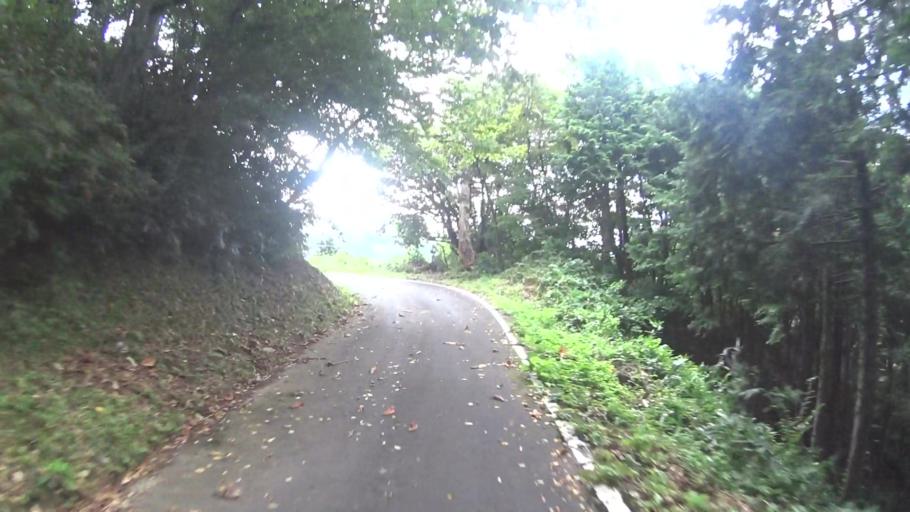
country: JP
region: Kyoto
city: Miyazu
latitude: 35.7336
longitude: 135.1933
